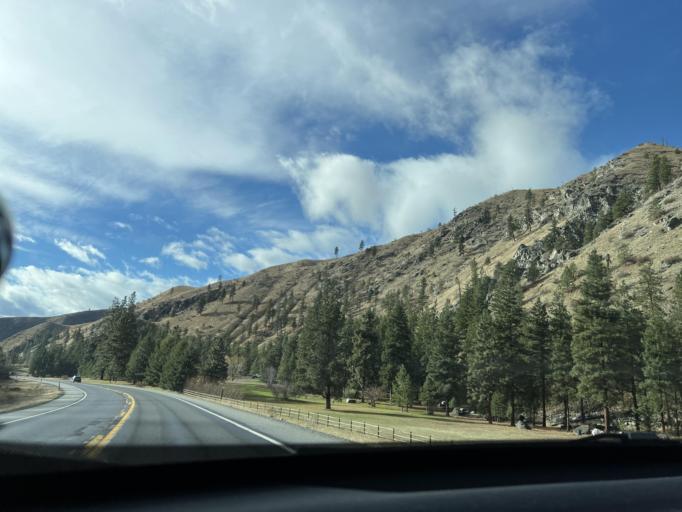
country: US
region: Washington
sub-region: Chelan County
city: Manson
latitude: 47.8197
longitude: -120.1287
